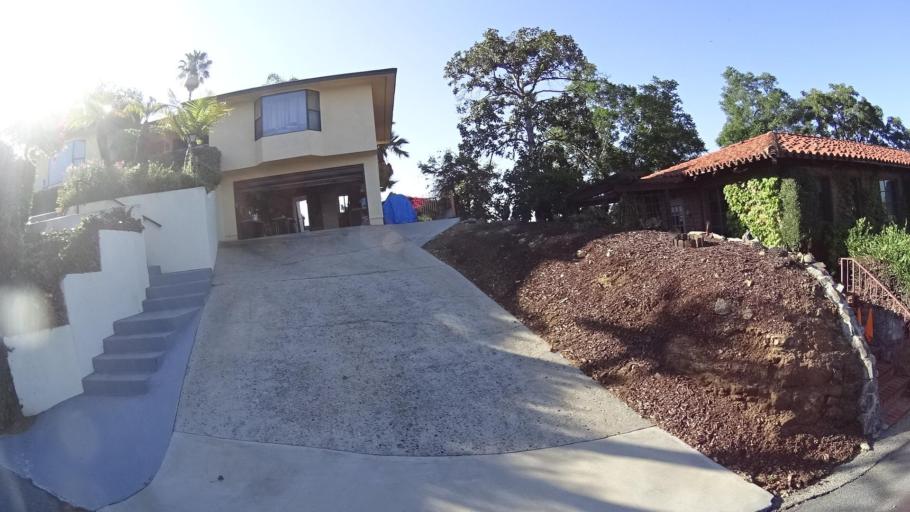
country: US
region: California
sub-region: San Diego County
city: Spring Valley
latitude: 32.7618
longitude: -116.9983
